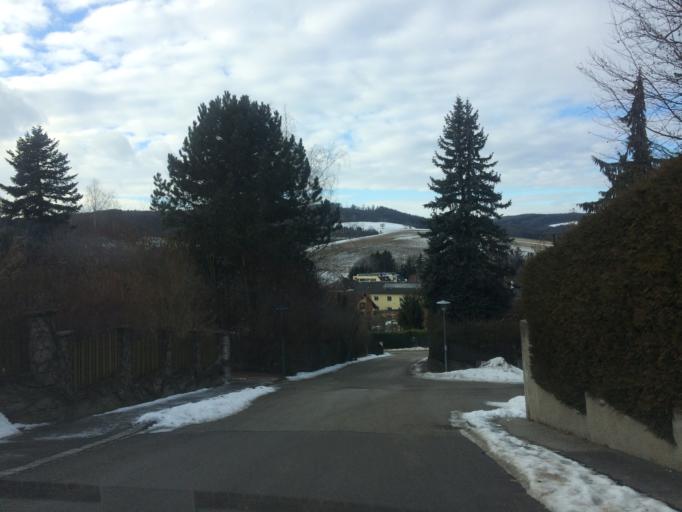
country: AT
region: Lower Austria
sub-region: Politischer Bezirk Wien-Umgebung
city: Gablitz
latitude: 48.2311
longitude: 16.1518
